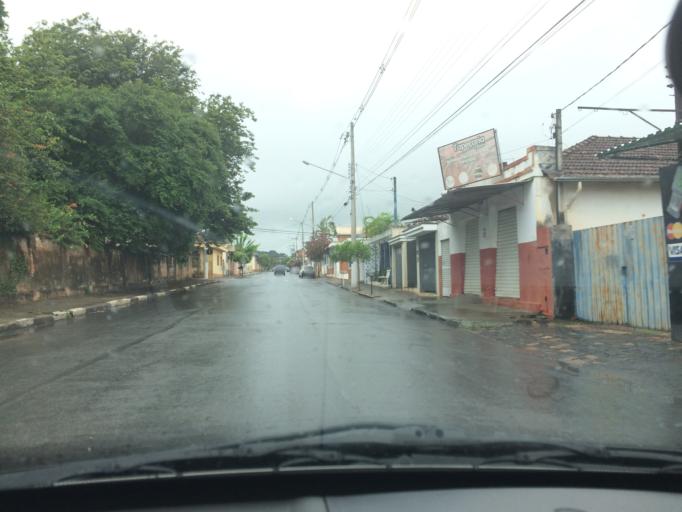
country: BR
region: Sao Paulo
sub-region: Casa Branca
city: Casa Branca
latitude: -21.7772
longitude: -47.0838
